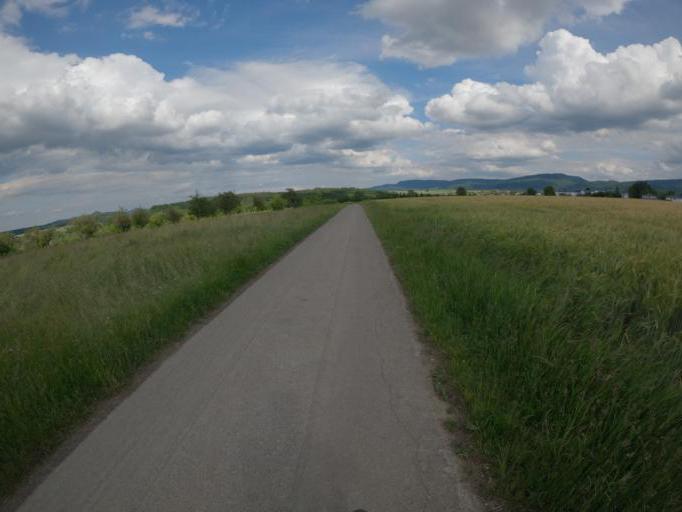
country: DE
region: Baden-Wuerttemberg
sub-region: Regierungsbezirk Stuttgart
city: Hattenhofen
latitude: 48.6581
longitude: 9.5718
